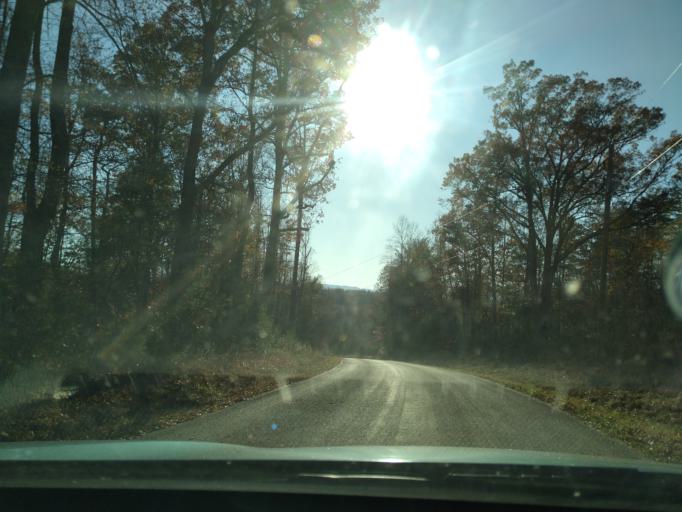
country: US
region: Virginia
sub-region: Floyd County
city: Floyd
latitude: 36.8315
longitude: -80.2004
